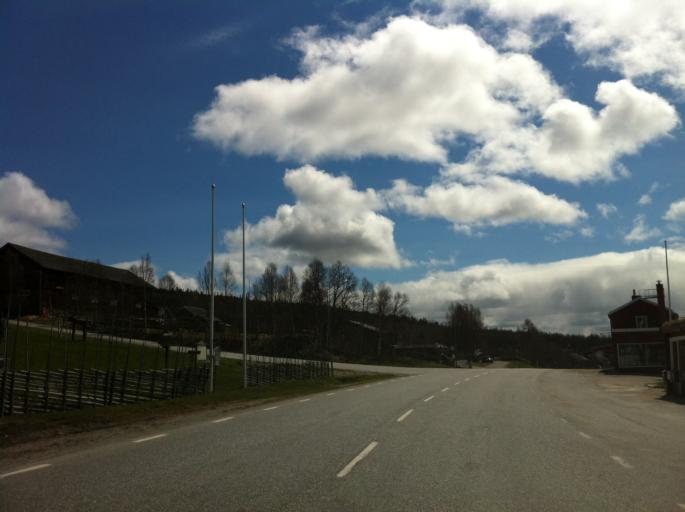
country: NO
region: Sor-Trondelag
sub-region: Tydal
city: Aas
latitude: 62.6383
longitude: 12.4428
